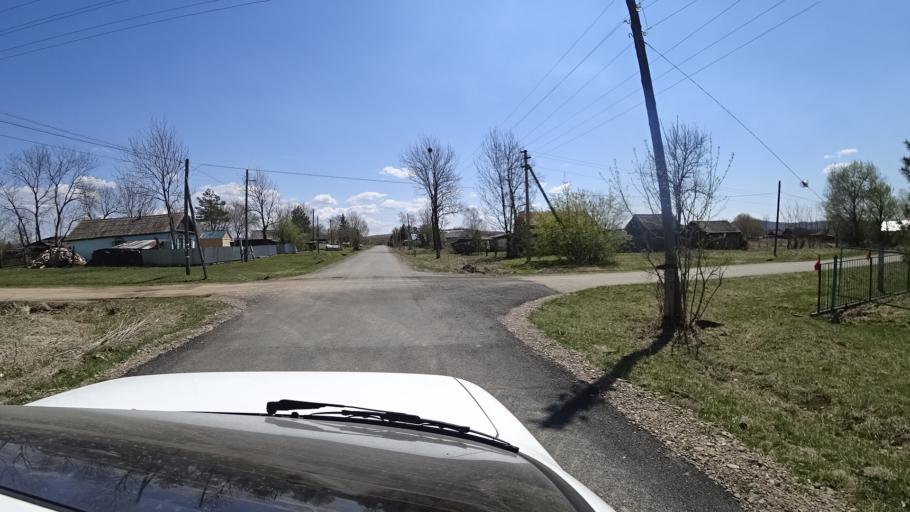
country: RU
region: Primorskiy
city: Dal'nerechensk
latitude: 45.7946
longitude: 133.7686
